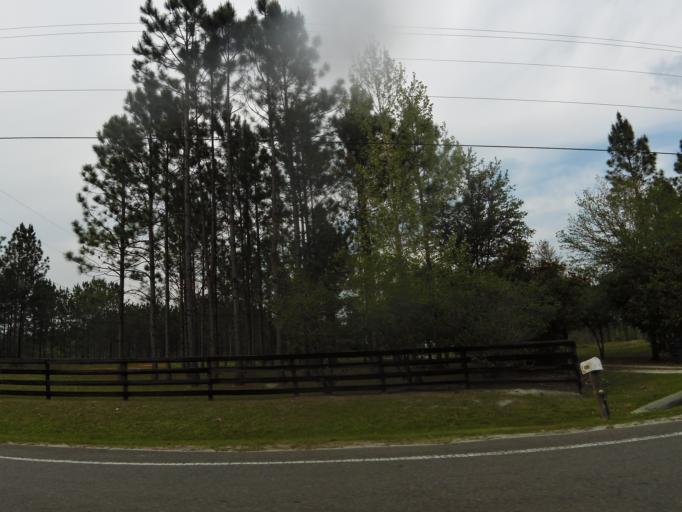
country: US
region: Florida
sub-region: Nassau County
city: Hilliard
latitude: 30.6978
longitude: -81.9031
